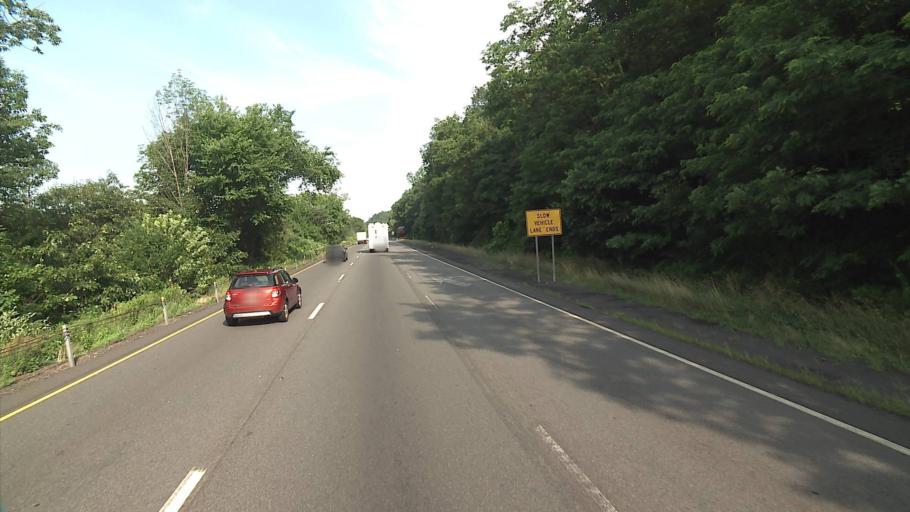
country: US
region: Connecticut
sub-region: New Haven County
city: Meriden
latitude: 41.5523
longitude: -72.8369
